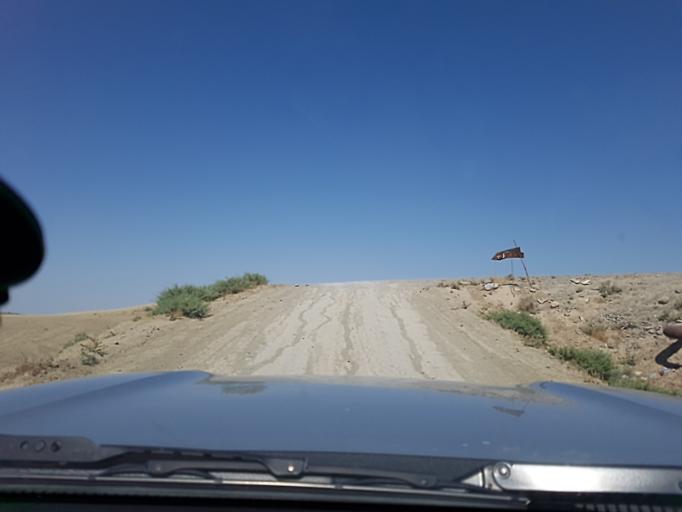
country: TM
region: Ahal
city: Baharly
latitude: 38.3972
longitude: 56.9793
